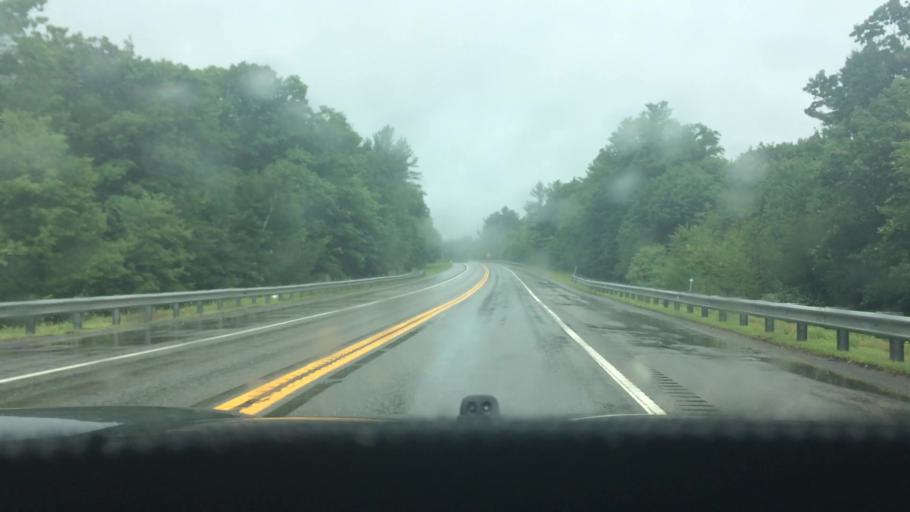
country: US
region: Massachusetts
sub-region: Worcester County
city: South Ashburnham
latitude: 42.5810
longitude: -71.9528
